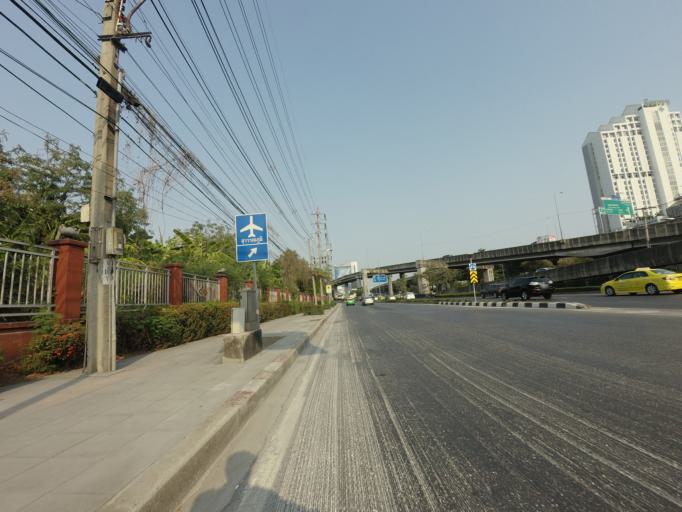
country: TH
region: Bangkok
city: Huai Khwang
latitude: 13.7553
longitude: 100.5789
